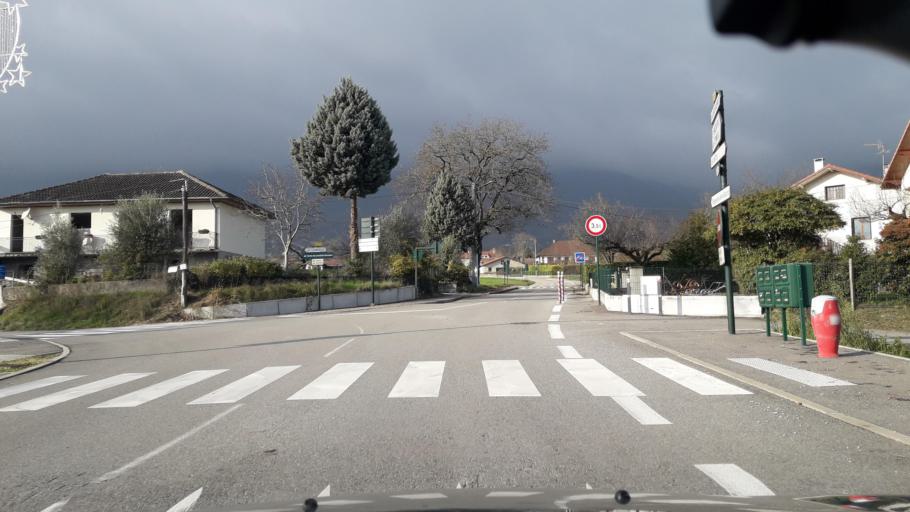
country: FR
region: Rhone-Alpes
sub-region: Departement de l'Isere
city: Saint-Nazaire-les-Eymes
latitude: 45.2426
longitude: 5.8445
